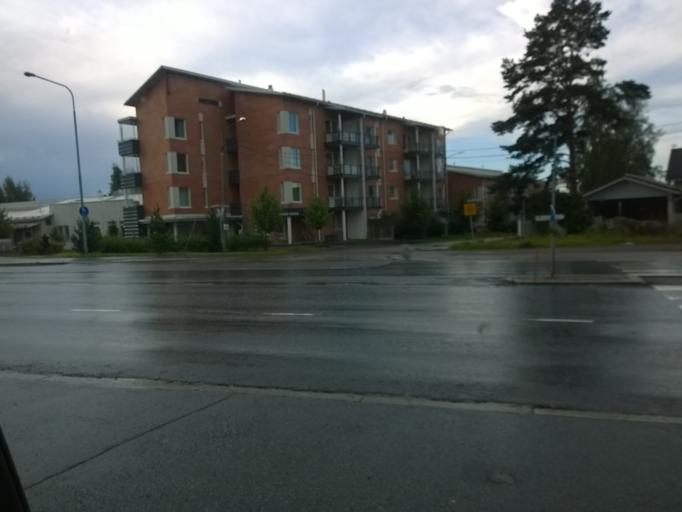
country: FI
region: Pirkanmaa
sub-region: Tampere
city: Tampere
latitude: 61.4865
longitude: 23.8335
